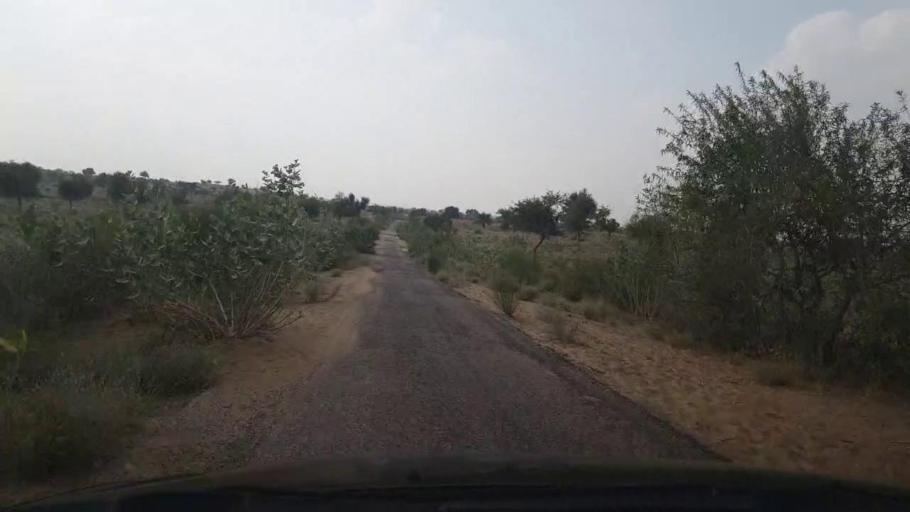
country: PK
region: Sindh
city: Islamkot
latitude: 24.9703
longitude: 70.5929
